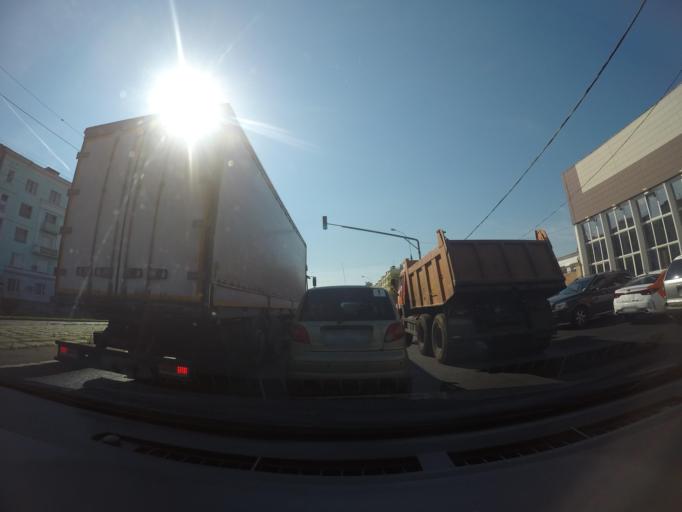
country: RU
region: Moscow
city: Lefortovo
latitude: 55.7744
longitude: 37.7241
